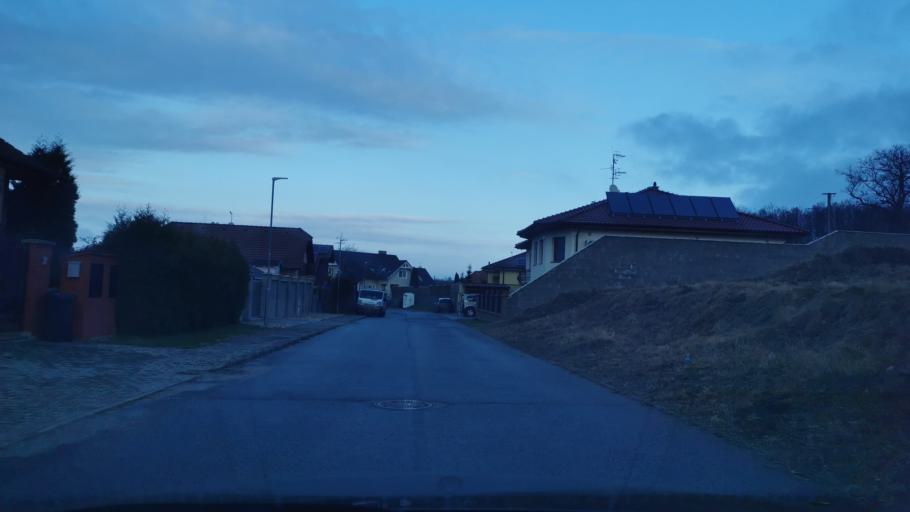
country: SK
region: Trnavsky
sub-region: Okres Skalica
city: Holic
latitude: 48.7989
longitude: 17.1658
